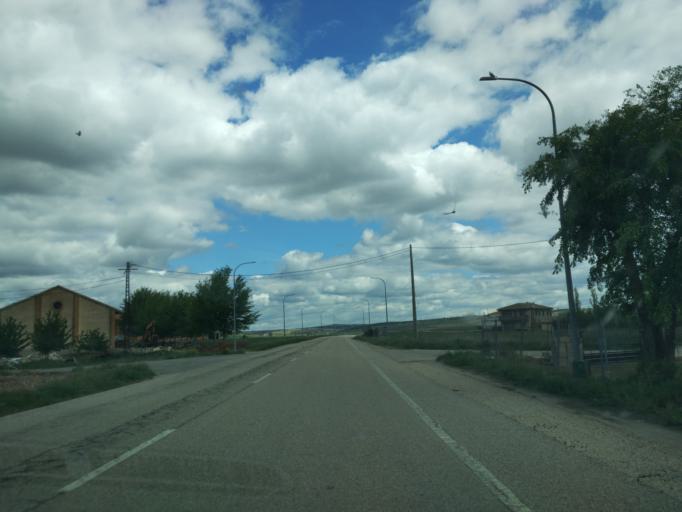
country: ES
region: Castille-La Mancha
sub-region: Provincia de Guadalajara
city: Torremocha del Campo
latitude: 40.9792
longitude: -2.6171
